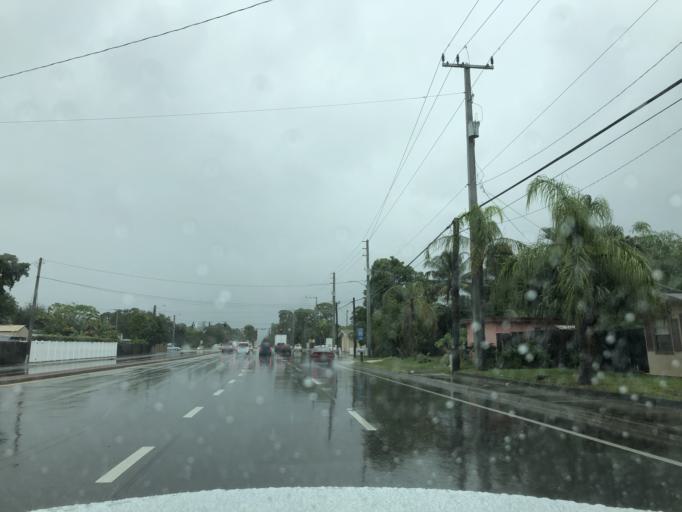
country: US
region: Florida
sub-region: Palm Beach County
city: Haverhill
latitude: 26.6907
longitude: -80.1198
